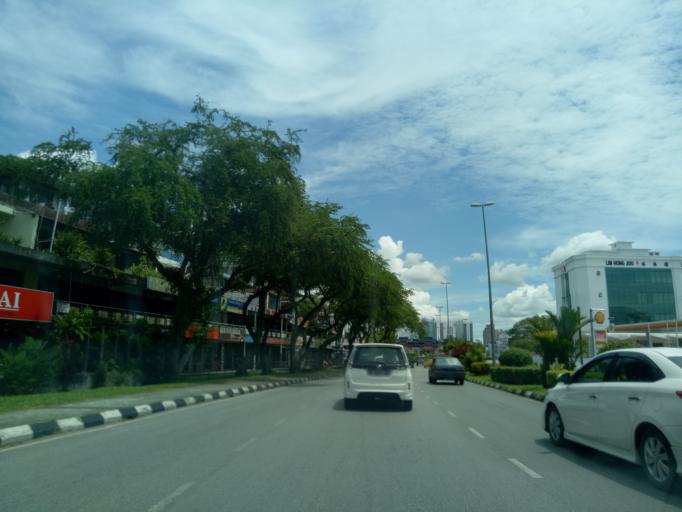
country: MY
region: Sarawak
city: Kuching
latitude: 1.5525
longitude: 110.3608
